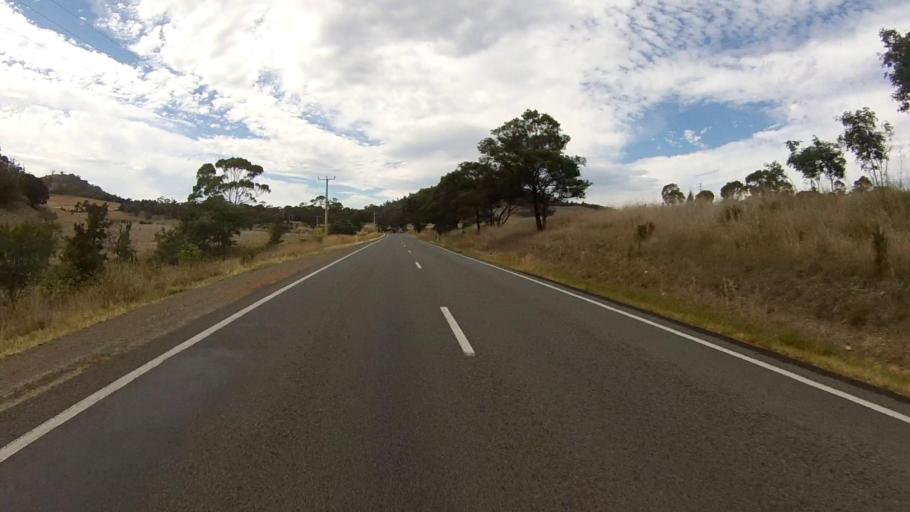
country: AU
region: Tasmania
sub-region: Sorell
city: Sorell
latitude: -42.6982
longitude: 147.4840
